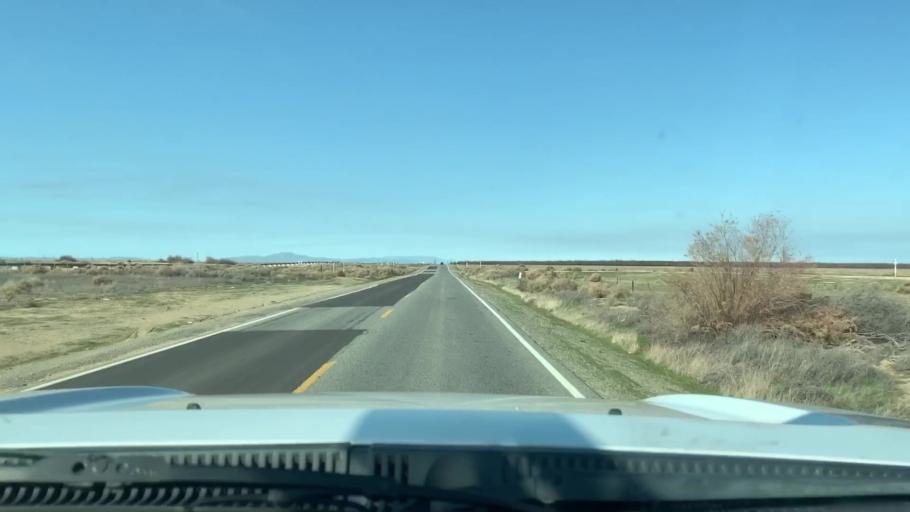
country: US
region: California
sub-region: Kern County
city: Lost Hills
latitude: 35.5503
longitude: -119.7881
